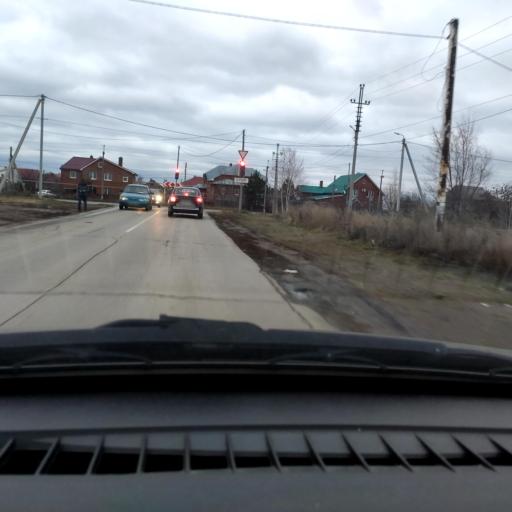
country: RU
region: Samara
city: Podstepki
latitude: 53.5224
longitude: 49.1839
